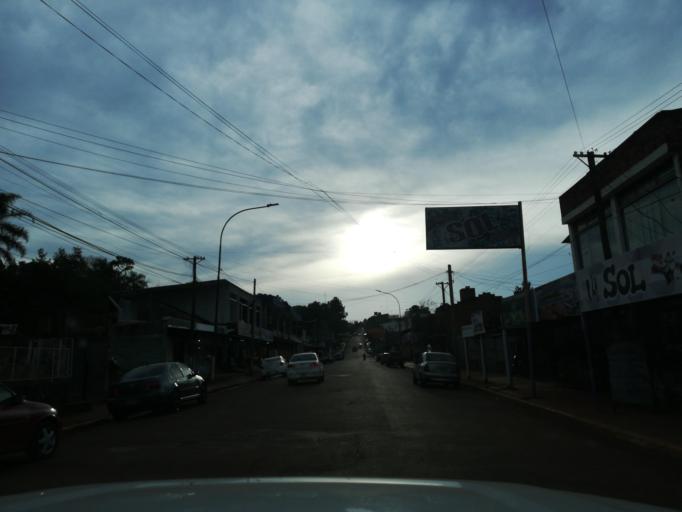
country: AR
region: Misiones
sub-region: Departamento de San Pedro
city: San Pedro
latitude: -26.6238
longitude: -54.1119
